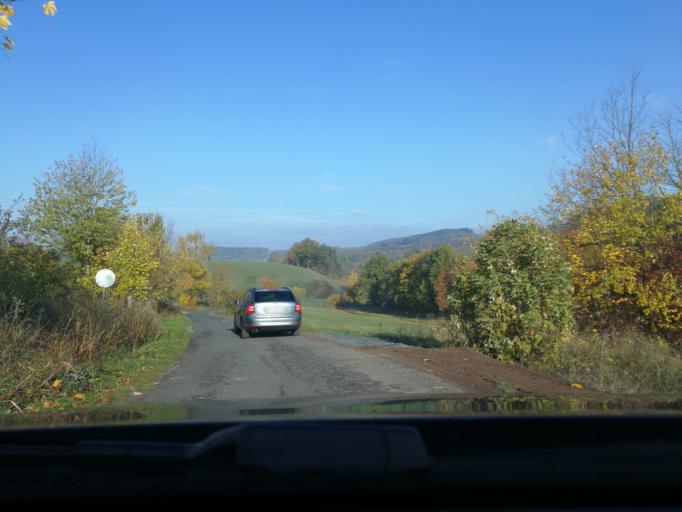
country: DE
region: Hesse
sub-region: Regierungsbezirk Kassel
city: Poppenhausen
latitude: 50.4846
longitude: 9.8591
